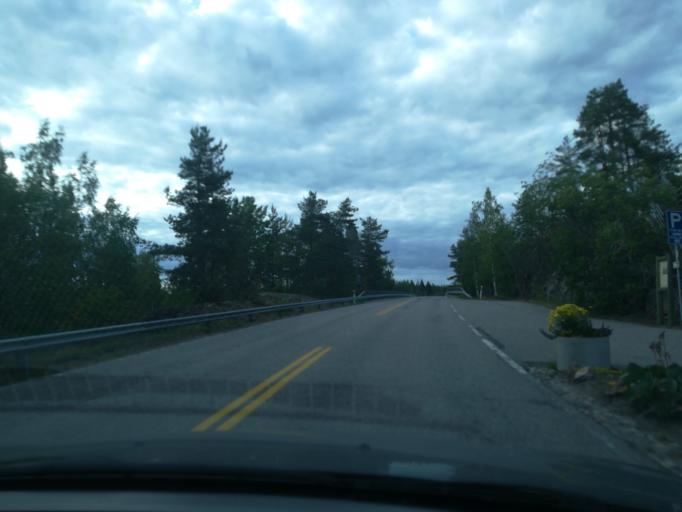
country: FI
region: Southern Savonia
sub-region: Mikkeli
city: Puumala
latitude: 61.5495
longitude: 27.9621
